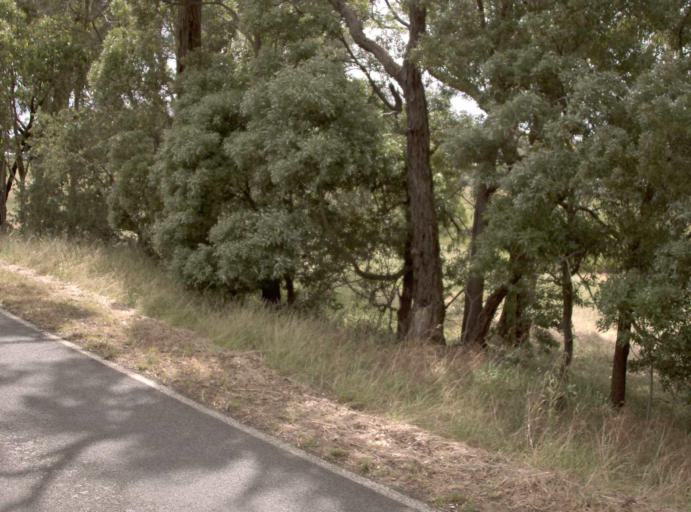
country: AU
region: Victoria
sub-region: Latrobe
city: Moe
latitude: -38.0732
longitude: 146.1741
